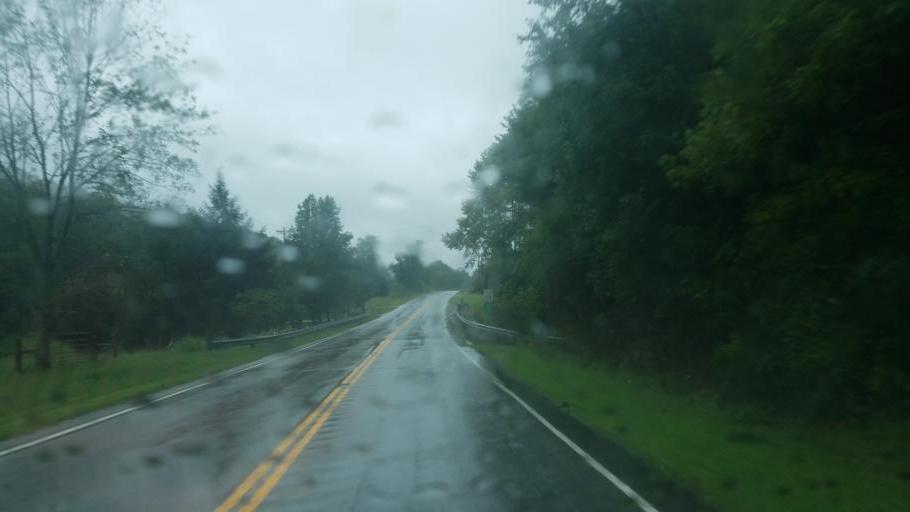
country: US
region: Kentucky
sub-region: Fleming County
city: Flemingsburg
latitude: 38.3326
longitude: -83.5924
